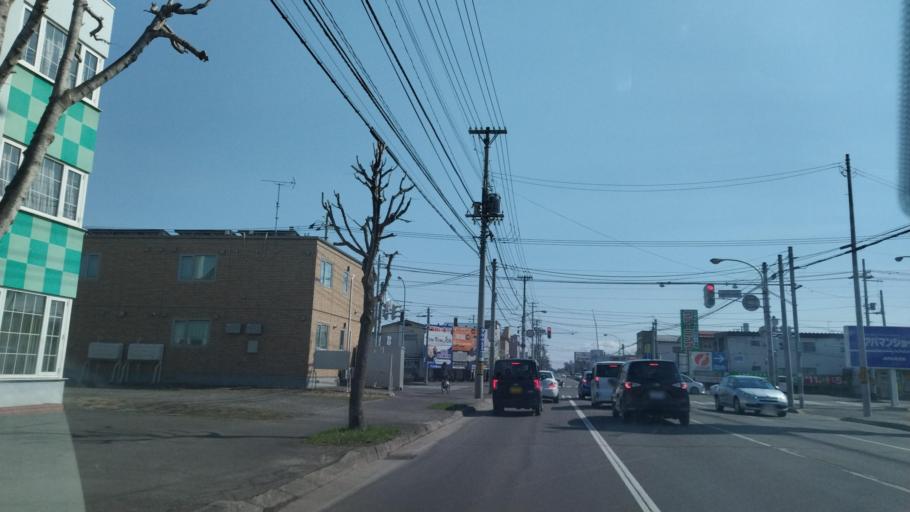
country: JP
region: Hokkaido
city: Obihiro
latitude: 42.8994
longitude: 143.2004
